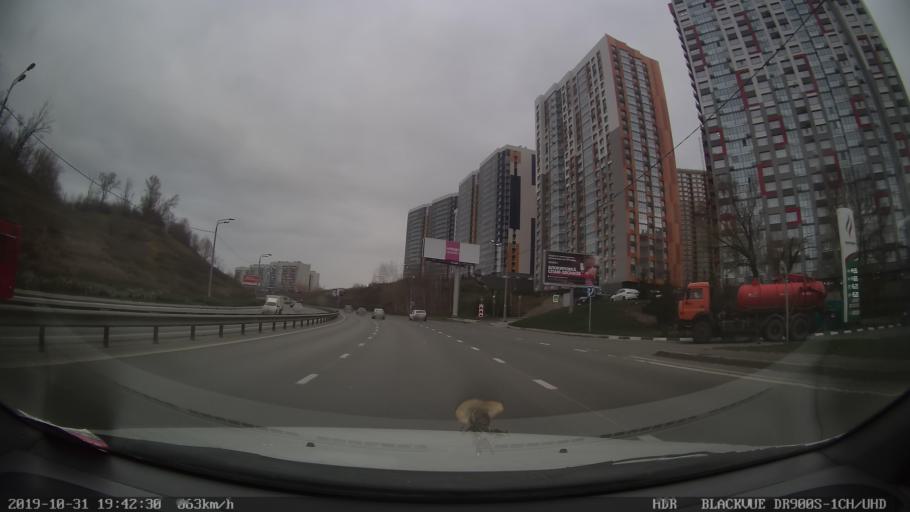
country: RU
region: Tatarstan
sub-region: Gorod Kazan'
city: Kazan
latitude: 55.7664
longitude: 49.1693
